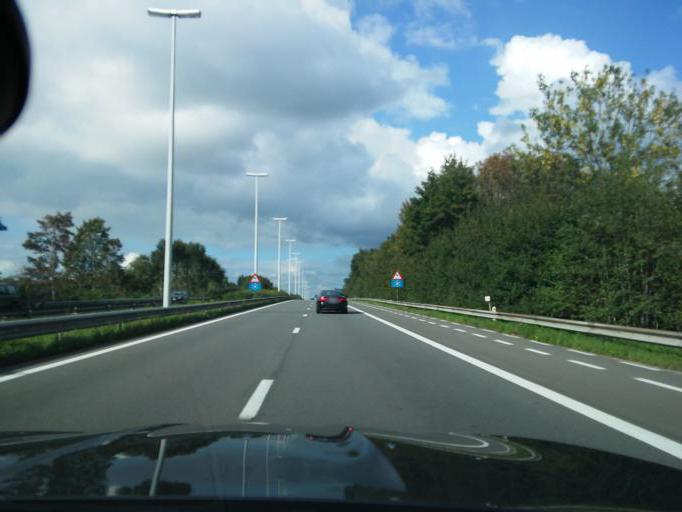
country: BE
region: Flanders
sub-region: Provincie Oost-Vlaanderen
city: Haaltert
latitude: 50.9034
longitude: 4.0327
